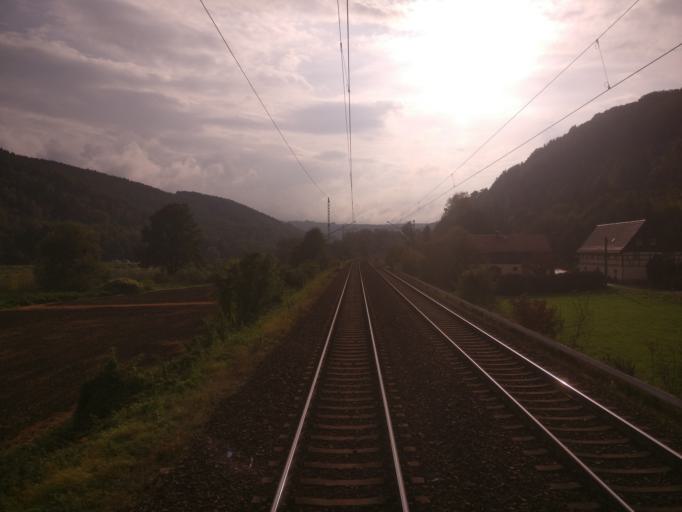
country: DE
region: Saxony
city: Konigstein
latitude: 50.9414
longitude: 14.0767
